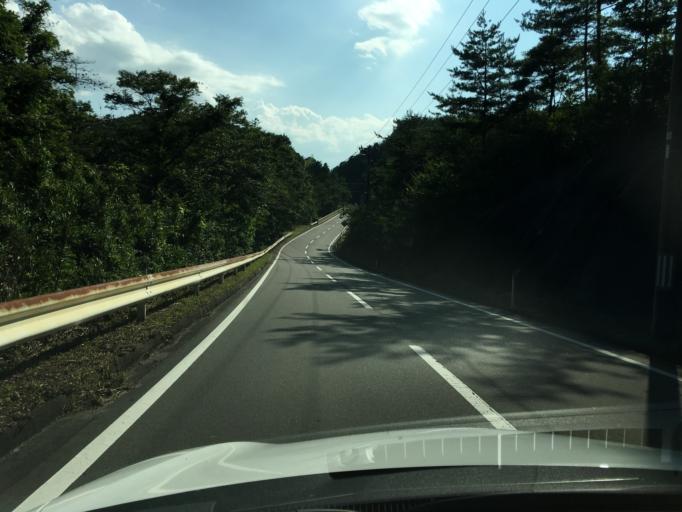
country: JP
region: Fukushima
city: Ishikawa
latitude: 37.1992
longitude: 140.5000
